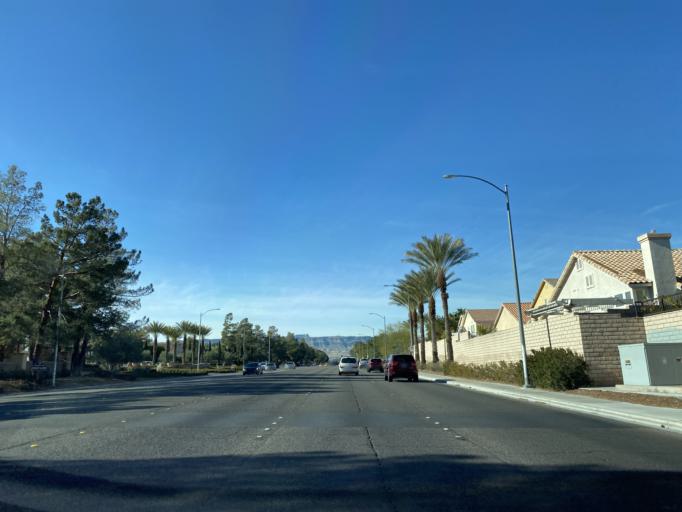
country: US
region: Nevada
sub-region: Clark County
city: Spring Valley
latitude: 36.0999
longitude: -115.2705
